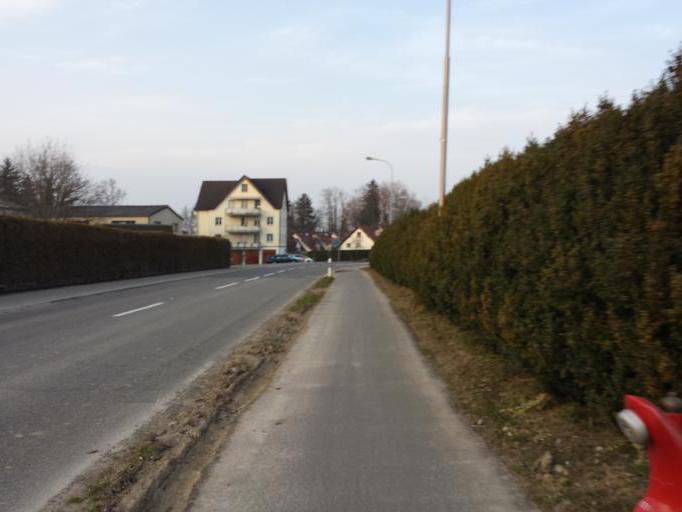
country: CH
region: Thurgau
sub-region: Arbon District
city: Egnach
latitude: 47.5399
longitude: 9.3773
